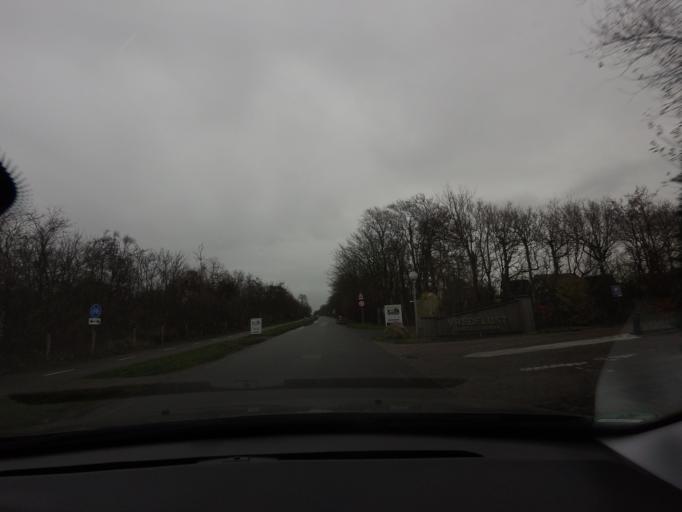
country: NL
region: North Holland
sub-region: Gemeente Texel
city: Den Burg
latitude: 53.0760
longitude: 4.7571
